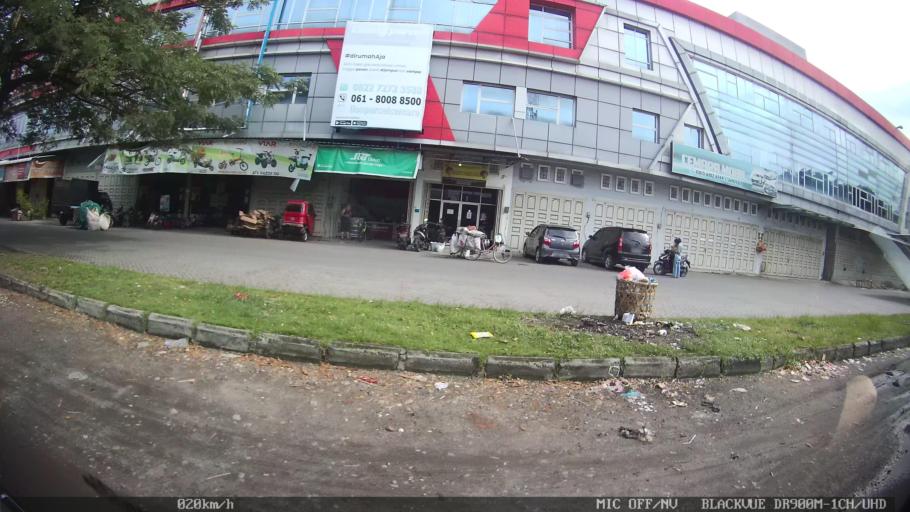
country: ID
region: North Sumatra
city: Medan
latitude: 3.6294
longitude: 98.6990
